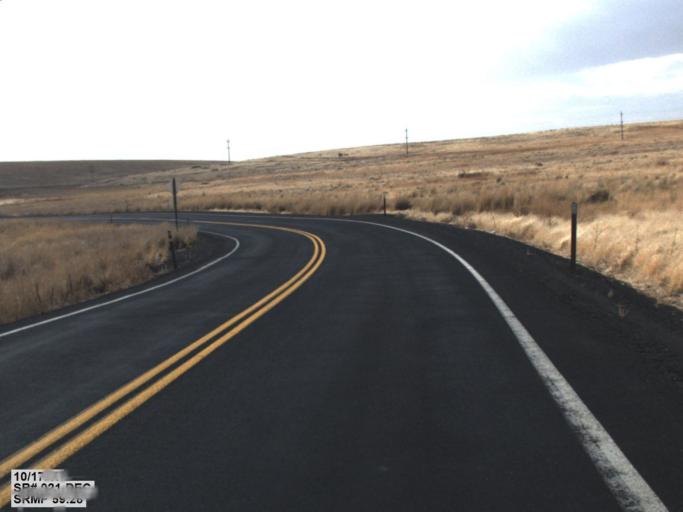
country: US
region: Washington
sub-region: Adams County
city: Ritzville
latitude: 47.3777
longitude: -118.6942
